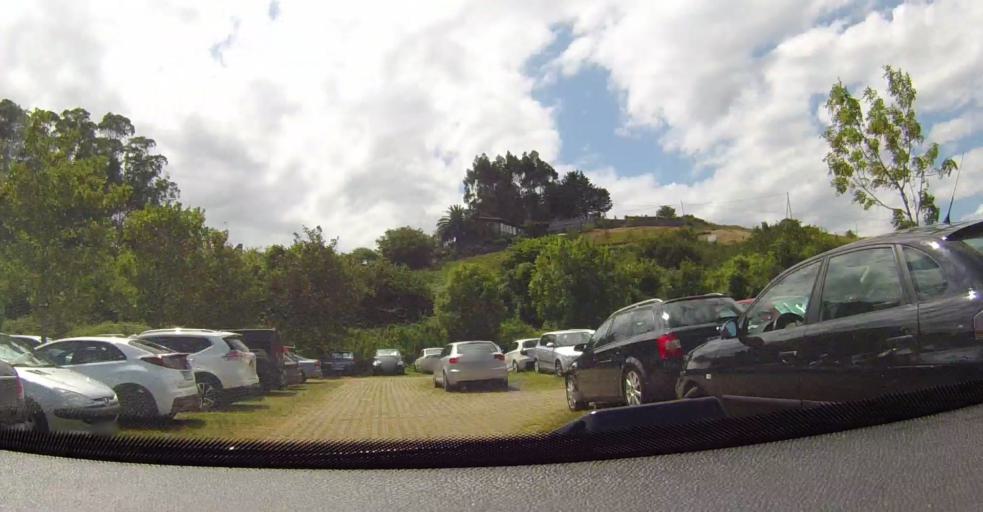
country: ES
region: Asturias
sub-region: Province of Asturias
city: Villaviciosa
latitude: 43.5318
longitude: -5.3740
